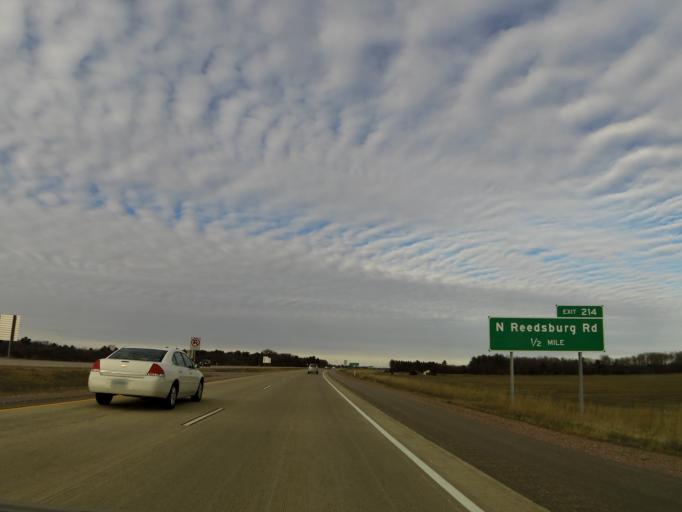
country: US
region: Wisconsin
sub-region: Sauk County
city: West Baraboo
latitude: 43.5215
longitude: -89.7867
